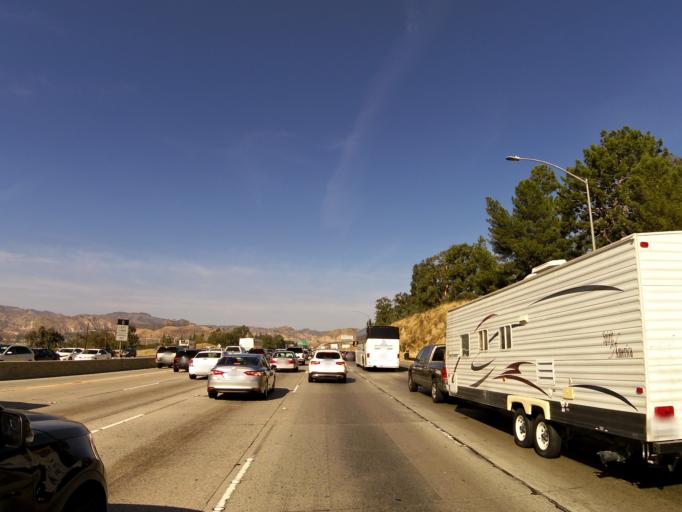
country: US
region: California
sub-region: Los Angeles County
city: San Fernando
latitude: 34.3054
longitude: -118.4815
